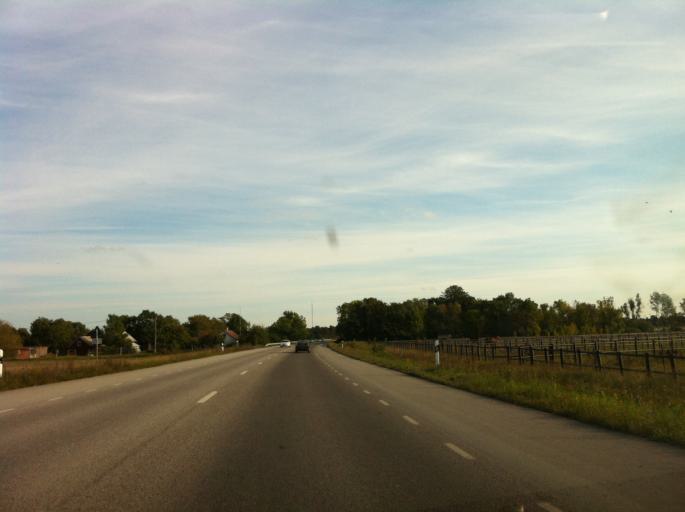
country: SE
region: Gotland
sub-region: Gotland
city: Visby
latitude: 57.6215
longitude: 18.3286
